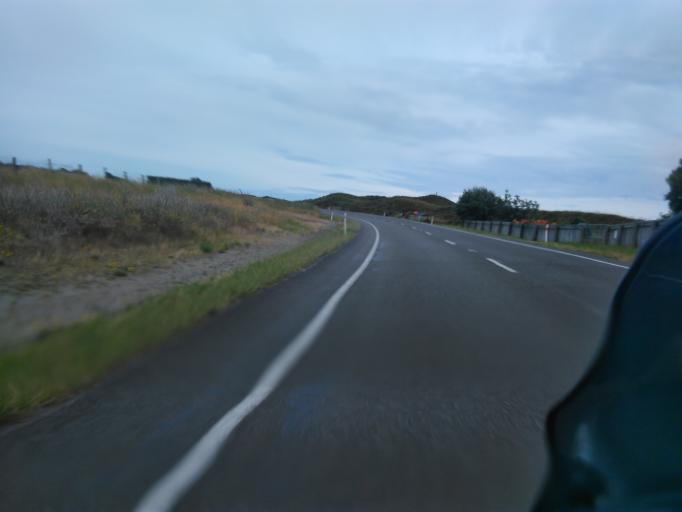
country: NZ
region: Bay of Plenty
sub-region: Opotiki District
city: Opotiki
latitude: -37.9863
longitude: 177.3796
